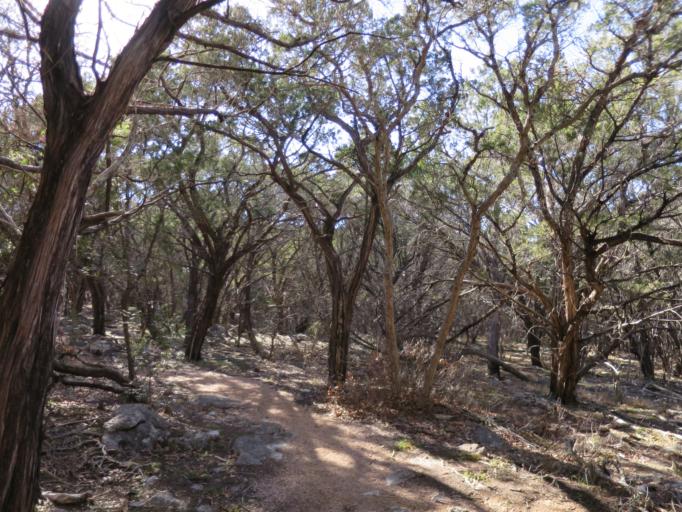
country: US
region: Texas
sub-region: Llano County
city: Kingsland
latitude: 30.6856
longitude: -98.3549
